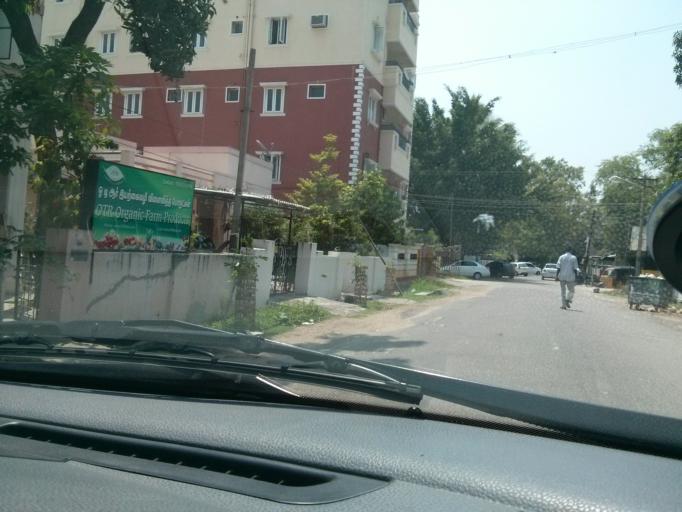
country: IN
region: Tamil Nadu
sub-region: Coimbatore
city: Coimbatore
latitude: 11.0250
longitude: 76.9456
